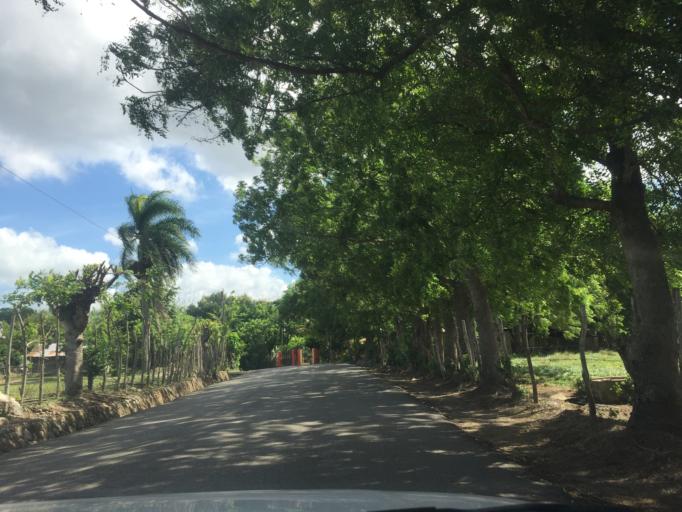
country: DO
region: La Vega
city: Rio Verde Arriba
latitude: 19.3624
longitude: -70.5978
